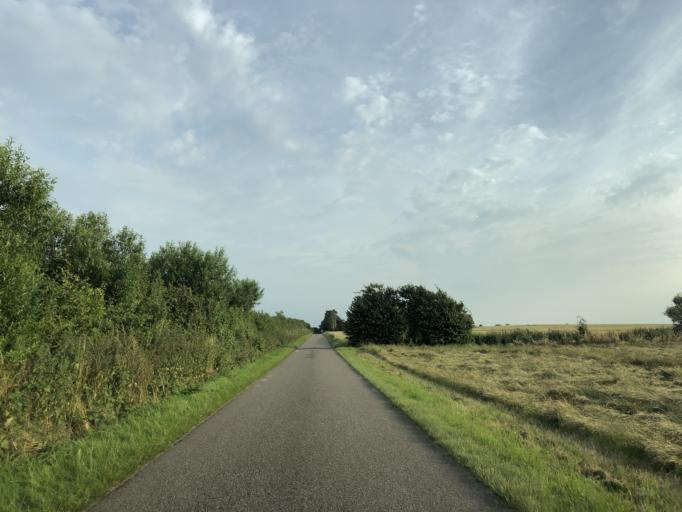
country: DK
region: South Denmark
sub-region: Vejle Kommune
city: Borkop
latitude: 55.5931
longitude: 9.6346
